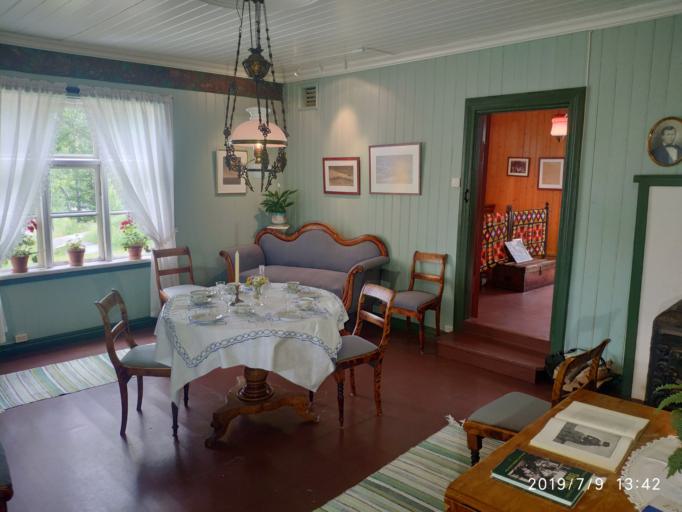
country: NO
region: Buskerud
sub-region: Sigdal
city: Prestfoss
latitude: 60.0618
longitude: 9.5052
